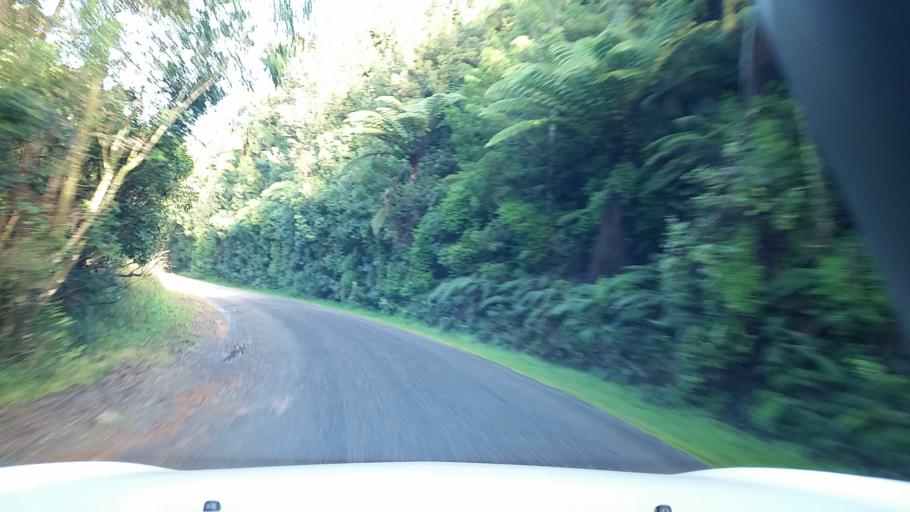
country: NZ
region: Waikato
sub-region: Matamata-Piako District
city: Matamata
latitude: -37.8159
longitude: 175.6331
